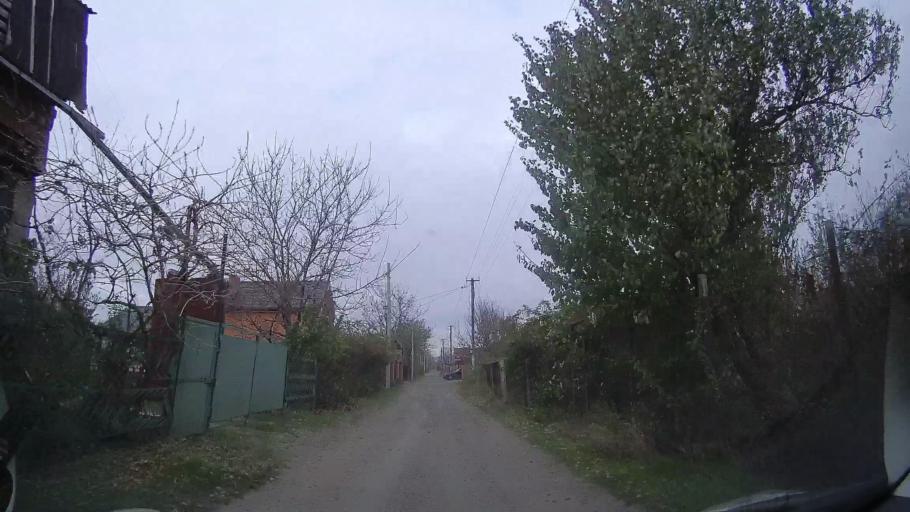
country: RU
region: Rostov
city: Bataysk
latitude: 47.0833
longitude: 39.7602
